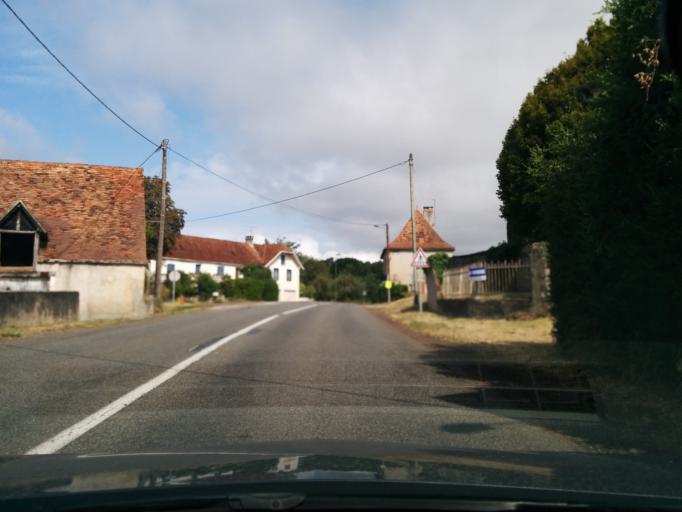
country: FR
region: Midi-Pyrenees
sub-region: Departement du Lot
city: Pradines
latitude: 44.5599
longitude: 1.4735
